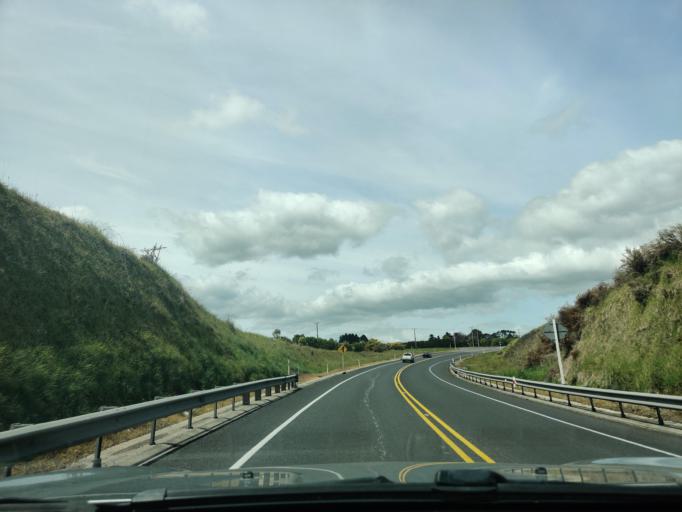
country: NZ
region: Taranaki
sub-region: New Plymouth District
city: New Plymouth
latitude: -39.2163
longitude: 174.2362
